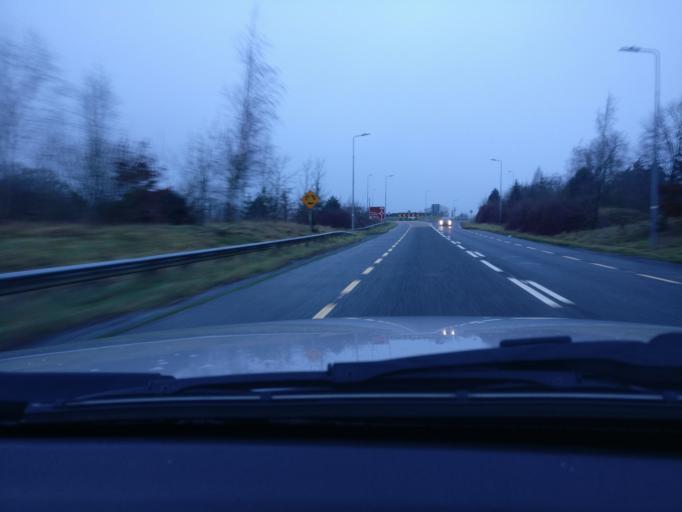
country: IE
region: Leinster
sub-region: An Iarmhi
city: Rochfortbridge
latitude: 53.3915
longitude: -7.3678
